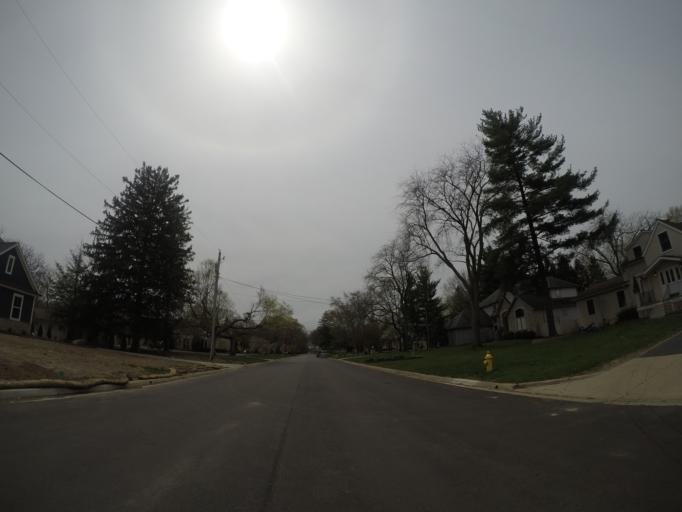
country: US
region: Ohio
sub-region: Franklin County
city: Upper Arlington
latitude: 40.0176
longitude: -83.0759
